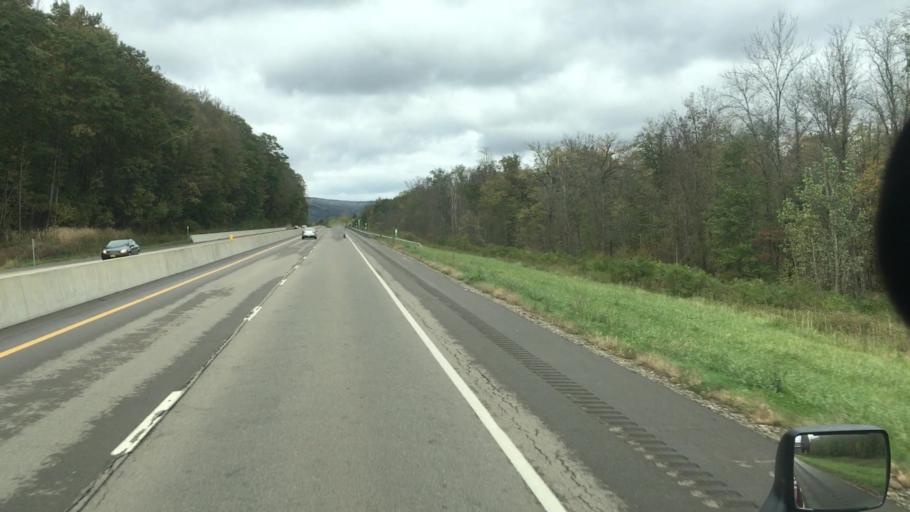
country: US
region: New York
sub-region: Cattaraugus County
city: Salamanca
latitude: 42.1091
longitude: -78.6630
